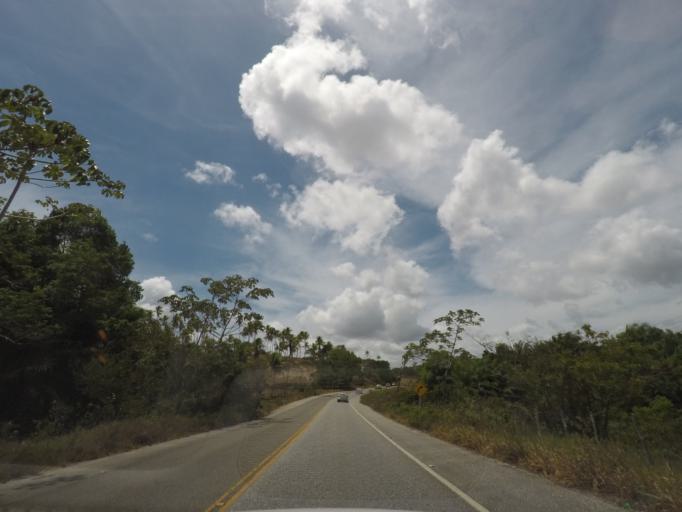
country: BR
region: Sergipe
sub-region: Indiaroba
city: Indiaroba
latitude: -11.4849
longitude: -37.4908
